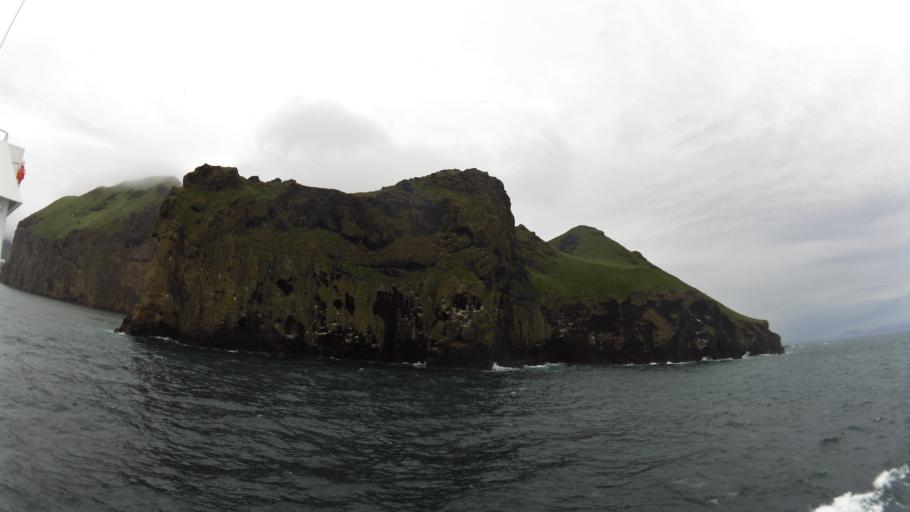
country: IS
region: South
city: Vestmannaeyjar
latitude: 63.4473
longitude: -20.2433
